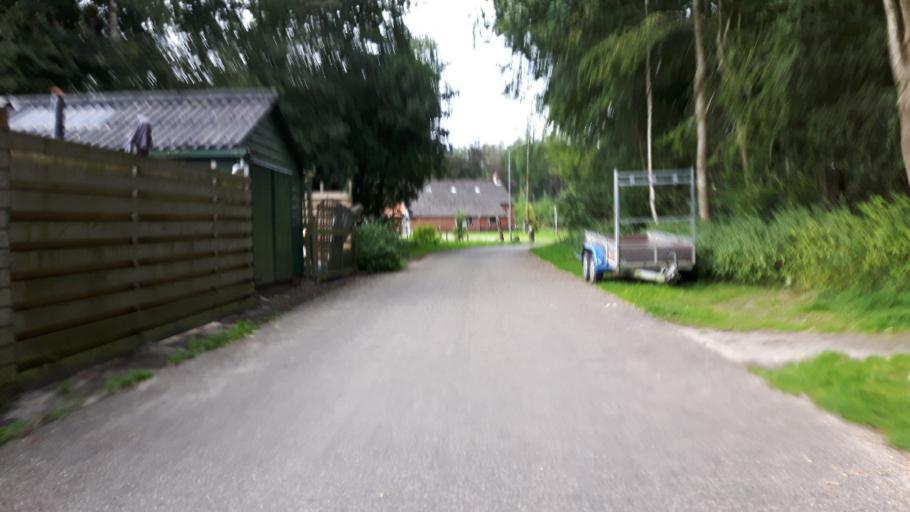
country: NL
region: Groningen
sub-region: Gemeente Leek
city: Leek
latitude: 53.1117
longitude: 6.4215
